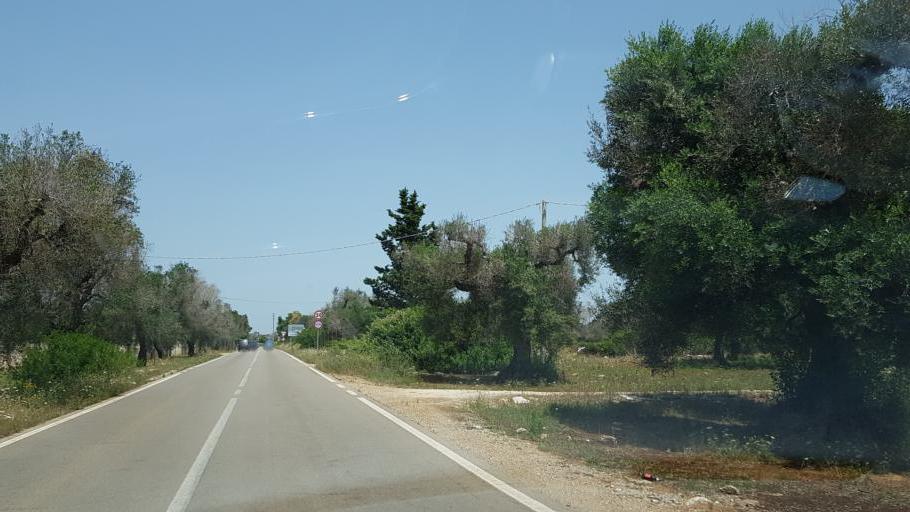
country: IT
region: Apulia
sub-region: Provincia di Lecce
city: Veglie
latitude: 40.3236
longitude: 17.9247
